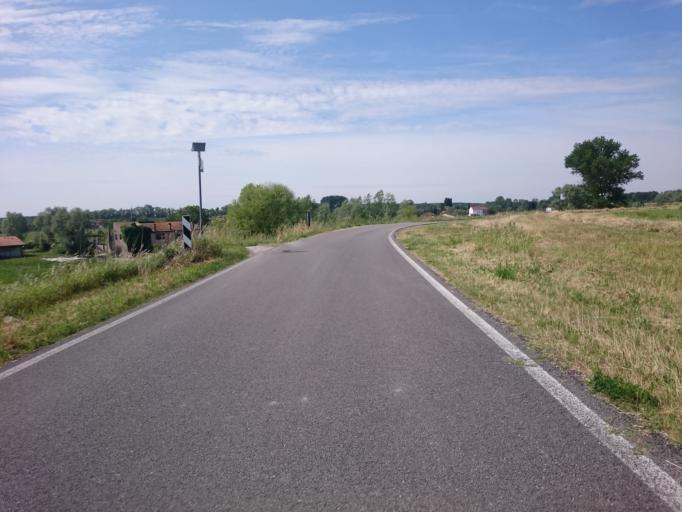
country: IT
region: Veneto
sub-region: Provincia di Rovigo
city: Corbola
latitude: 44.9795
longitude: 12.0829
